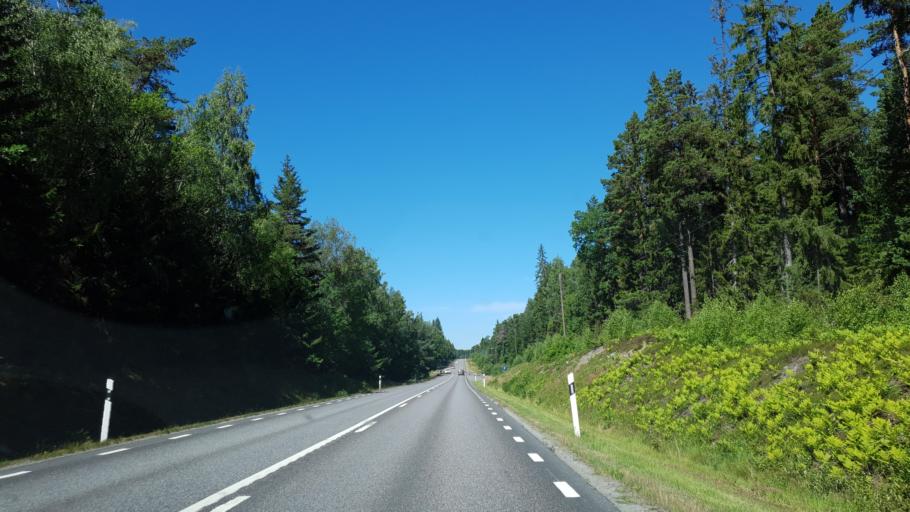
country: SE
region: Joenkoeping
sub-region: Varnamo Kommun
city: Bor
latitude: 57.0567
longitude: 14.2064
